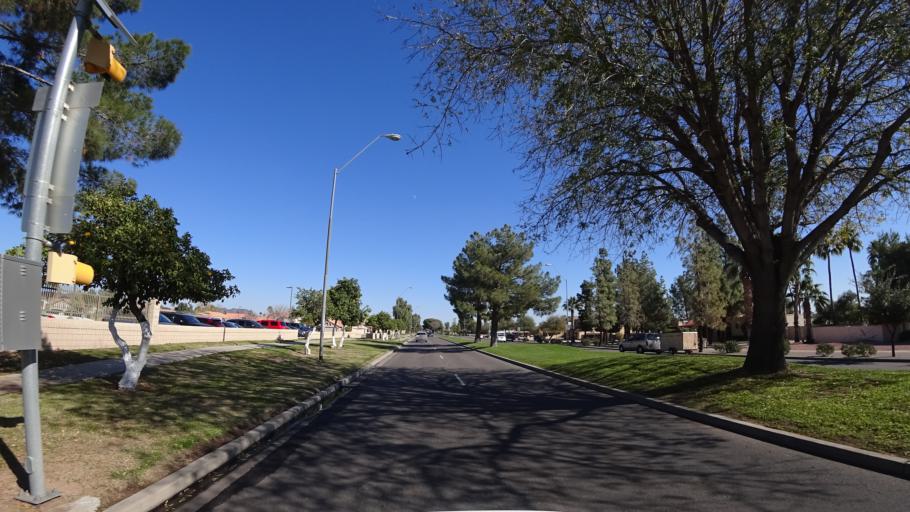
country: US
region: Arizona
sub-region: Maricopa County
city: Peoria
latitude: 33.6528
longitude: -112.2174
